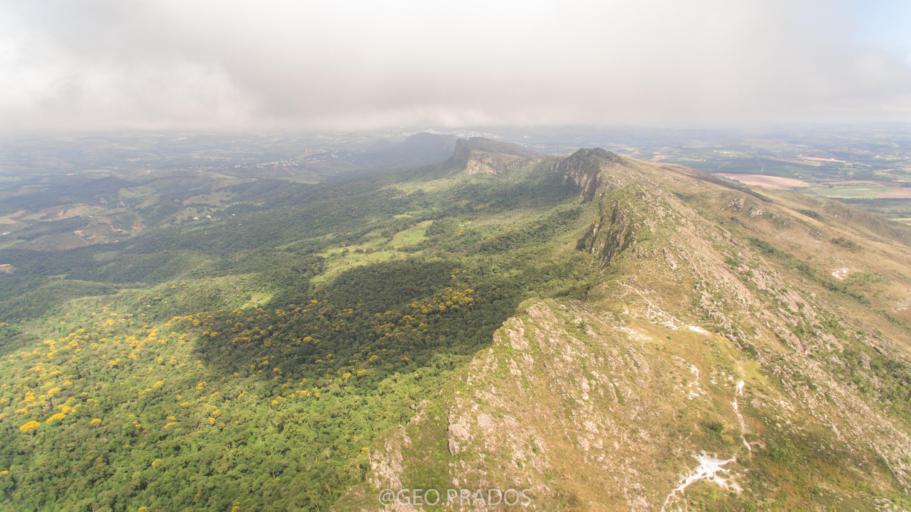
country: BR
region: Minas Gerais
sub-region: Tiradentes
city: Tiradentes
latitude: -21.0617
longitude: -44.1152
